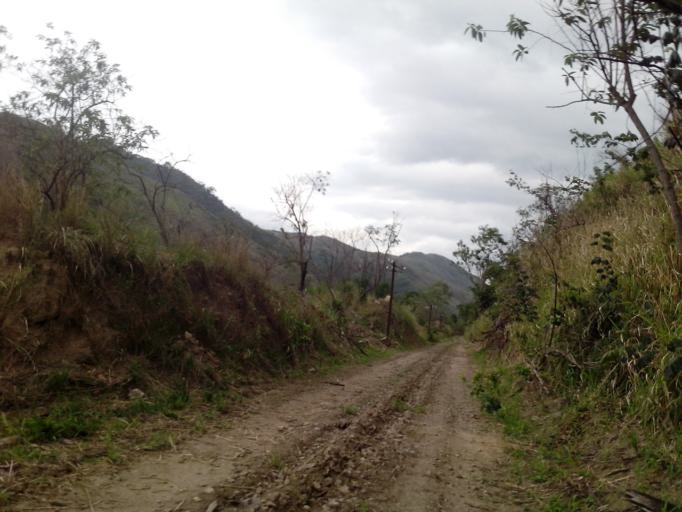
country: BR
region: Rio de Janeiro
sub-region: Miguel Pereira
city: Miguel Pereira
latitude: -22.5042
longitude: -43.5051
